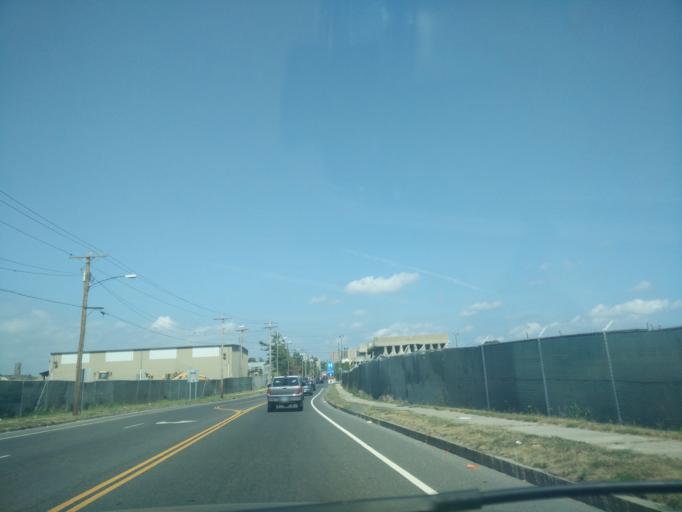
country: US
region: Connecticut
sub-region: Fairfield County
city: Bridgeport
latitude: 41.1792
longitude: -73.1727
